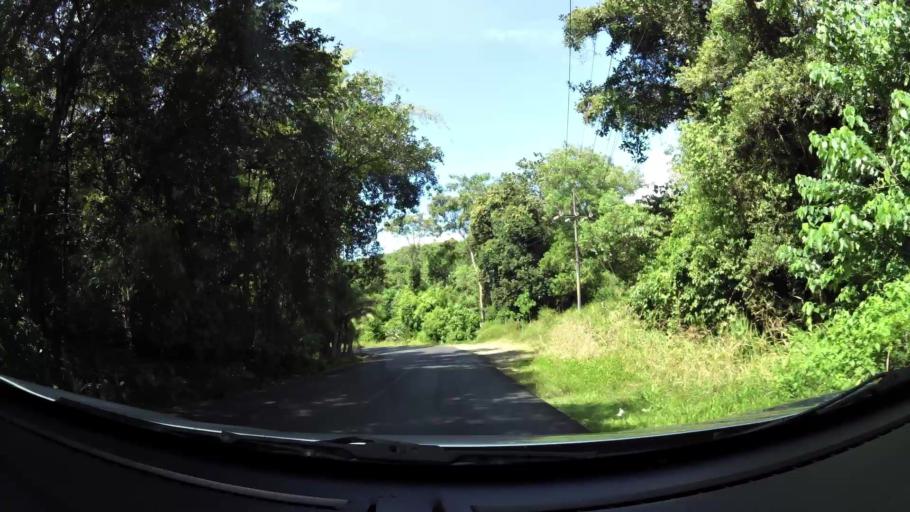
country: CR
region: San Jose
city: San Isidro
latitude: 9.2800
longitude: -83.8291
